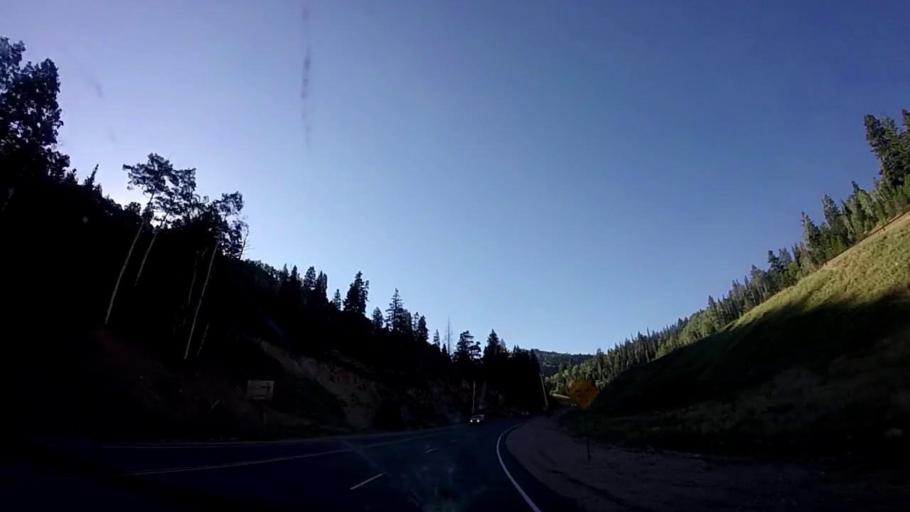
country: US
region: Utah
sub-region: Summit County
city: Park City
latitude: 40.6232
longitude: -111.4949
